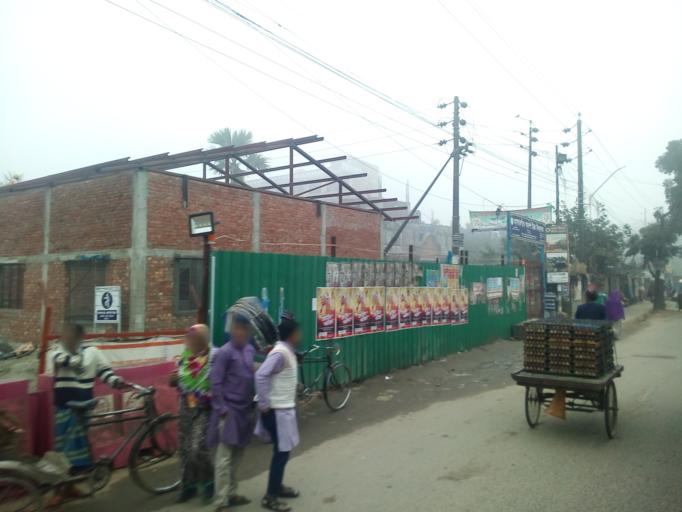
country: BD
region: Dhaka
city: Azimpur
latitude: 23.7815
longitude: 90.3789
